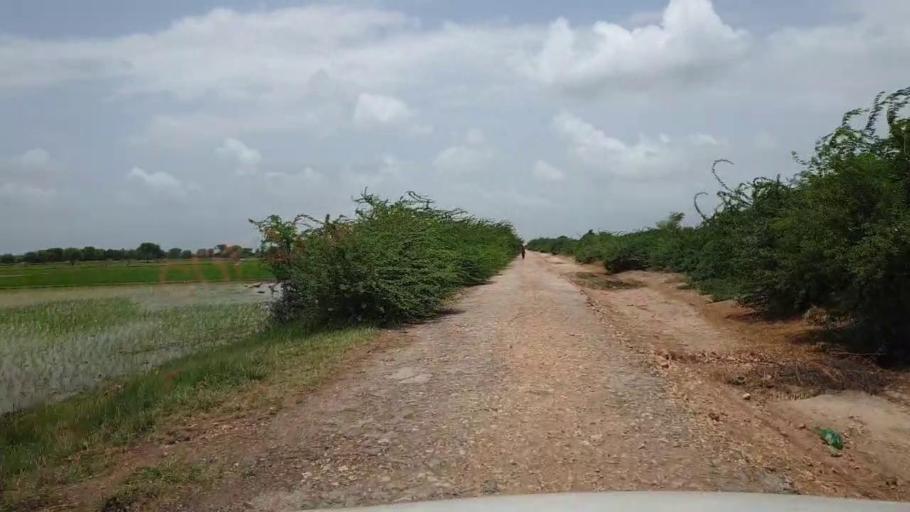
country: PK
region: Sindh
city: Kario
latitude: 24.7176
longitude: 68.5797
